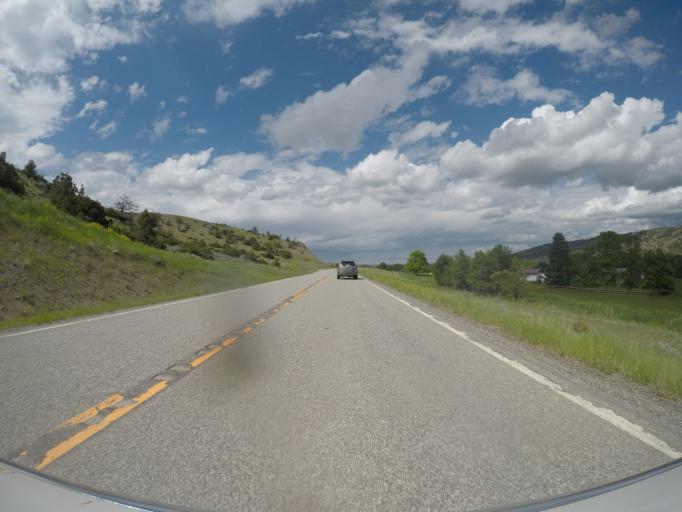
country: US
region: Montana
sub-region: Sweet Grass County
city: Big Timber
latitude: 45.7361
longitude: -109.9986
